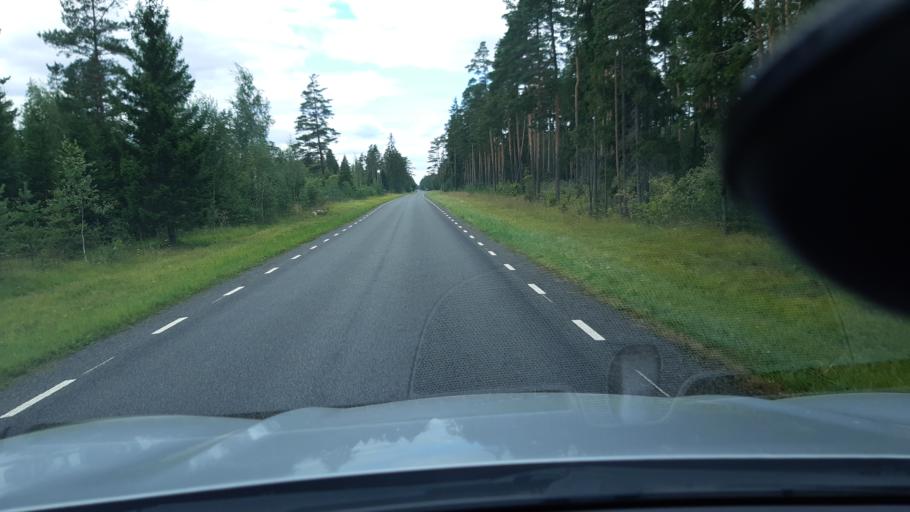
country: EE
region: Raplamaa
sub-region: Rapla vald
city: Rapla
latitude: 58.8935
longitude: 24.7078
